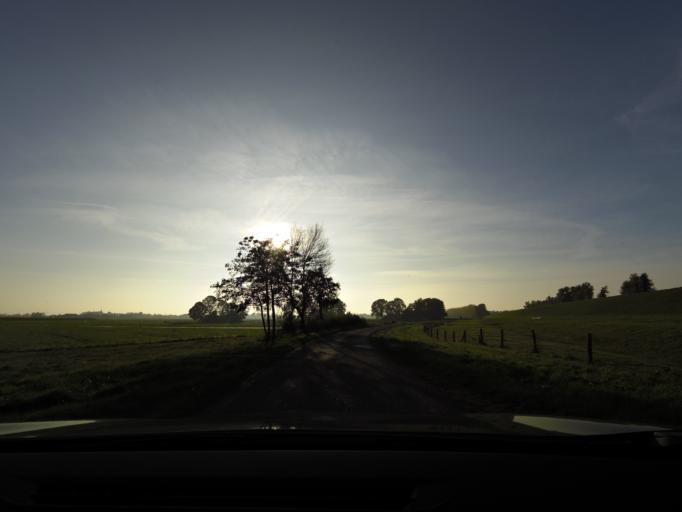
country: NL
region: North Brabant
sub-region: Gemeente Made en Drimmelen
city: Made
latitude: 51.7179
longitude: 4.7177
